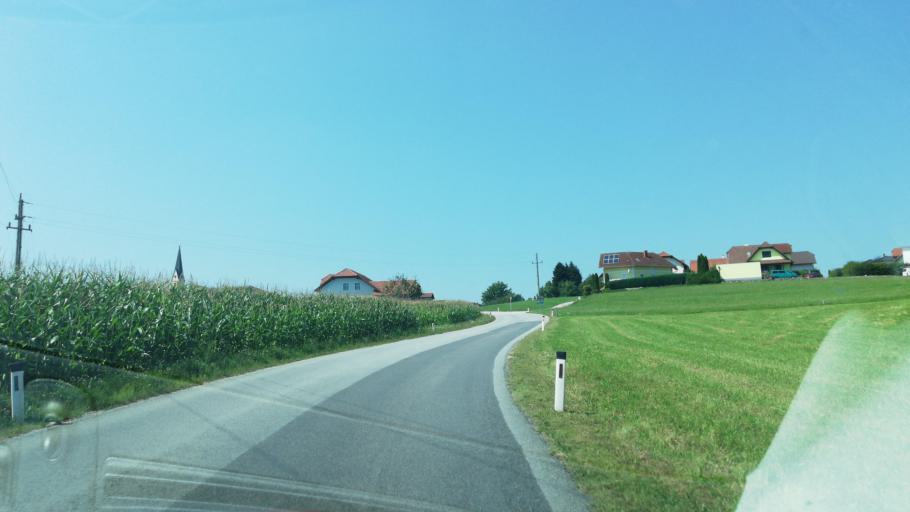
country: AT
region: Upper Austria
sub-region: Politischer Bezirk Urfahr-Umgebung
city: Feldkirchen an der Donau
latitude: 48.3394
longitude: 13.9632
